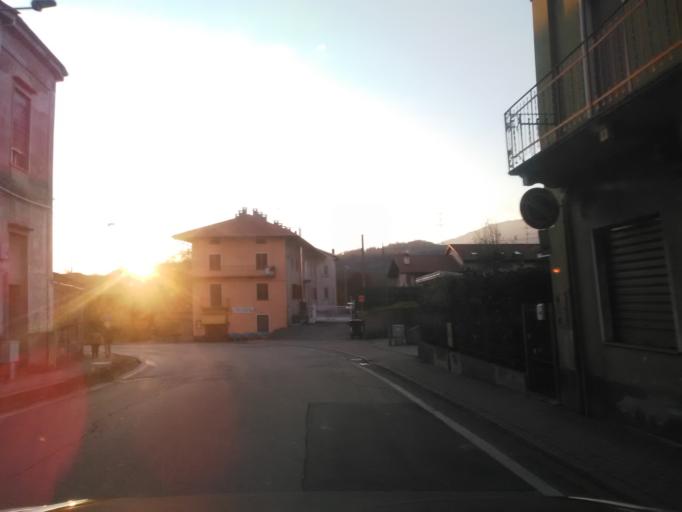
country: IT
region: Piedmont
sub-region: Provincia di Biella
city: Occhieppo Inferiore
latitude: 45.5536
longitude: 8.0175
